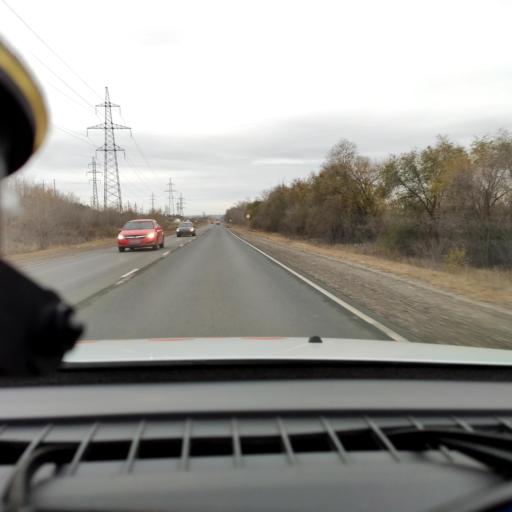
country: RU
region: Samara
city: Samara
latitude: 53.1207
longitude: 50.2151
